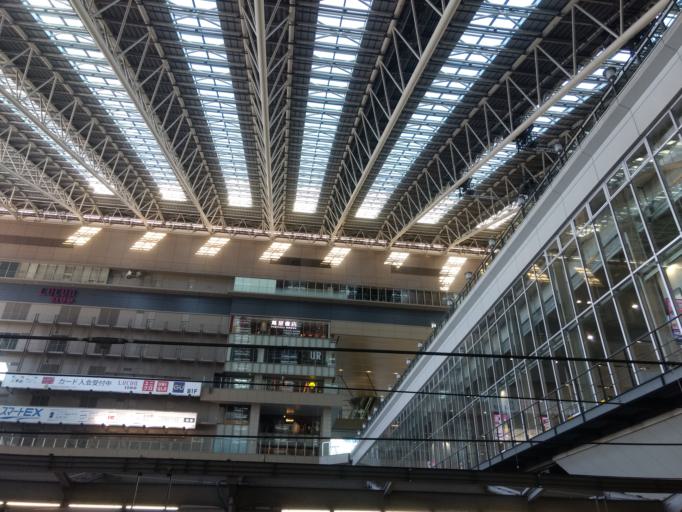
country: JP
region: Osaka
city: Osaka-shi
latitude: 34.7021
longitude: 135.4948
